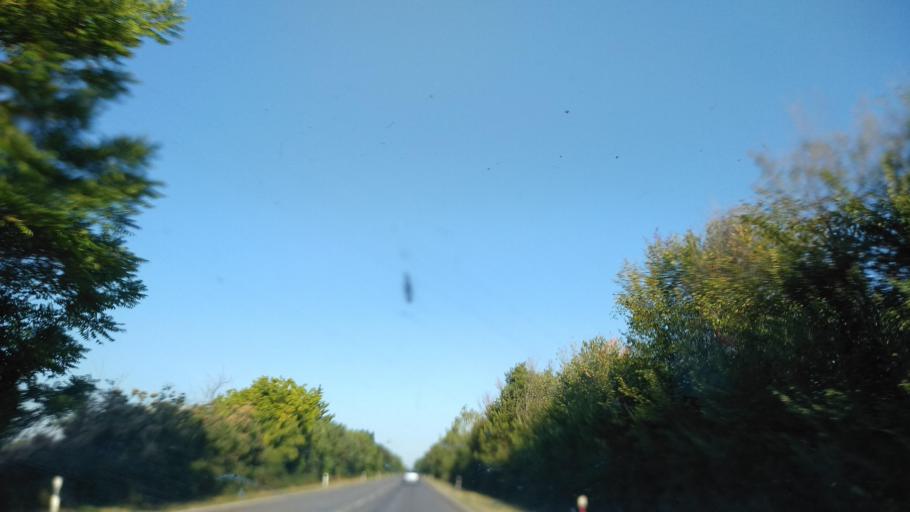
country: BG
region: Gabrovo
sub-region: Obshtina Dryanovo
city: Dryanovo
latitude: 43.0875
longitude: 25.4520
